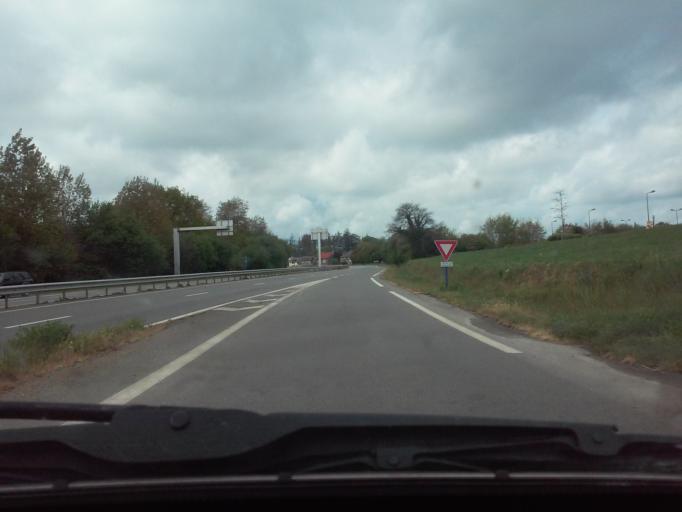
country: FR
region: Brittany
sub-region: Departement d'Ille-et-Vilaine
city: Dinard
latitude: 48.6134
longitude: -2.0602
